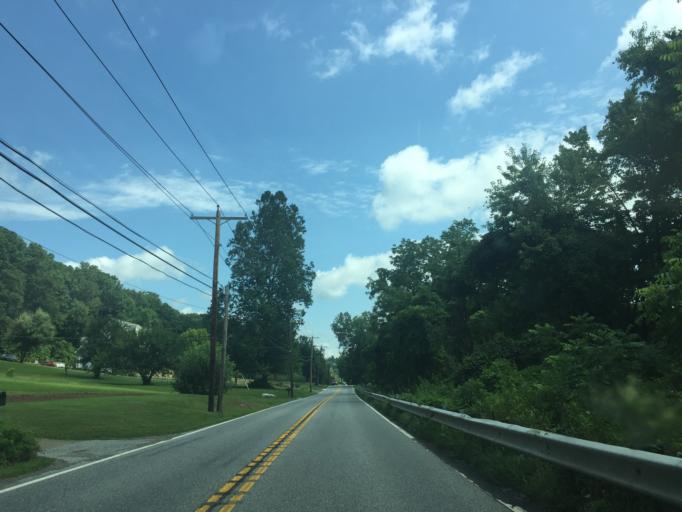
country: US
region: Maryland
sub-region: Baltimore County
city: Perry Hall
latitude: 39.4459
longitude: -76.4758
